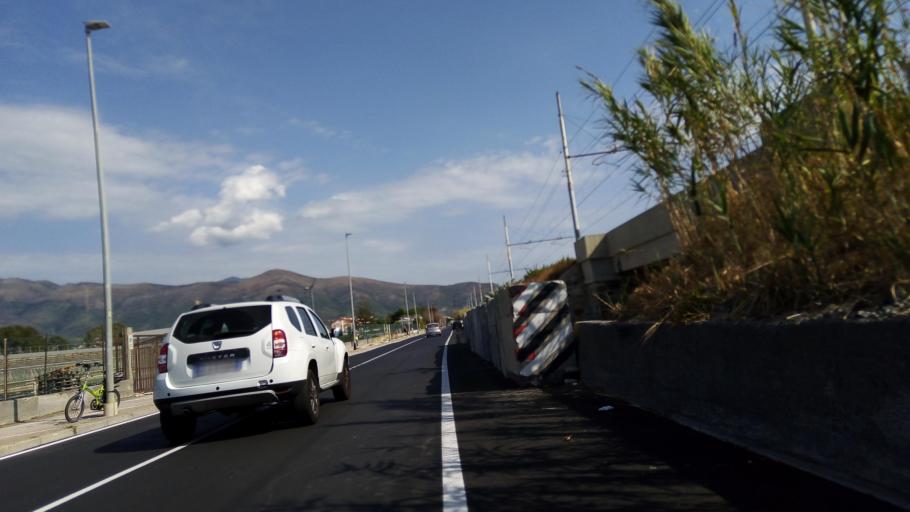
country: IT
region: Liguria
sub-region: Provincia di Savona
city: Albenga
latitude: 44.0658
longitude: 8.2249
